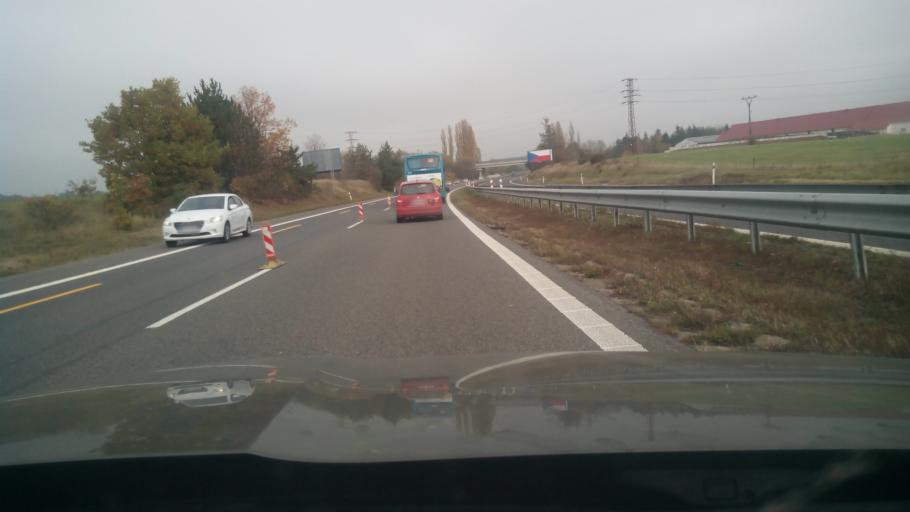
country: CZ
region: Central Bohemia
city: Dobris
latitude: 49.7400
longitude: 14.1427
